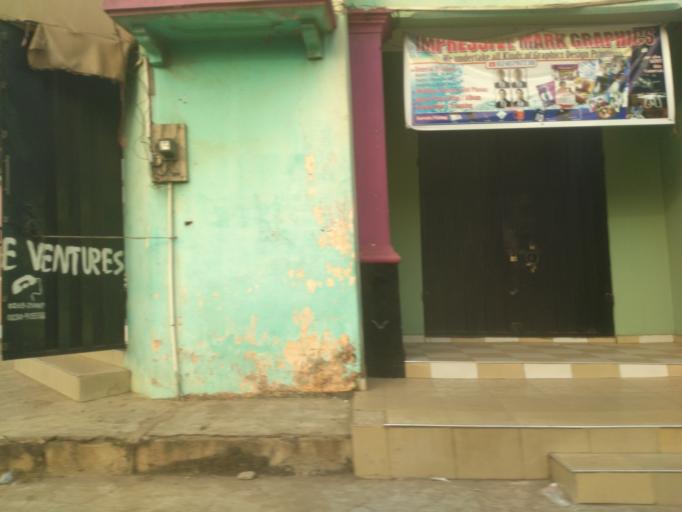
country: GH
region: Ashanti
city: Kumasi
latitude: 6.7033
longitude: -1.6171
